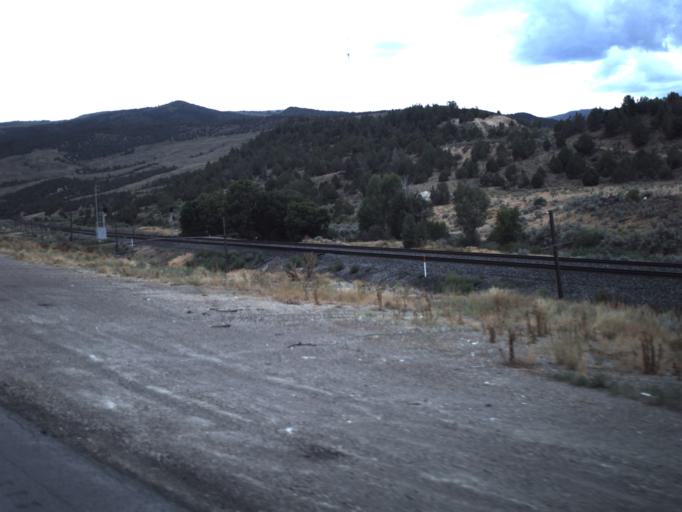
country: US
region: Utah
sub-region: Utah County
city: Mapleton
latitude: 39.9651
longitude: -111.3088
